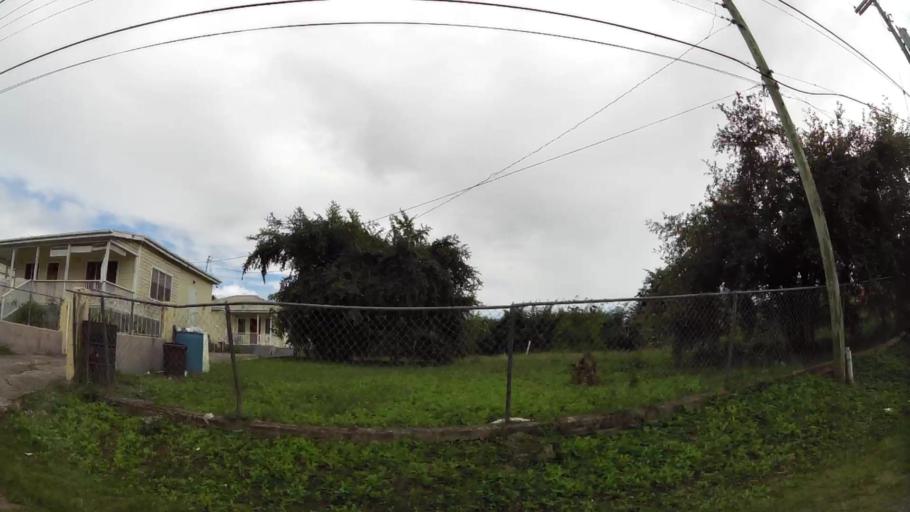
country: AG
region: Saint John
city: Potters Village
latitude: 17.0895
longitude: -61.8133
